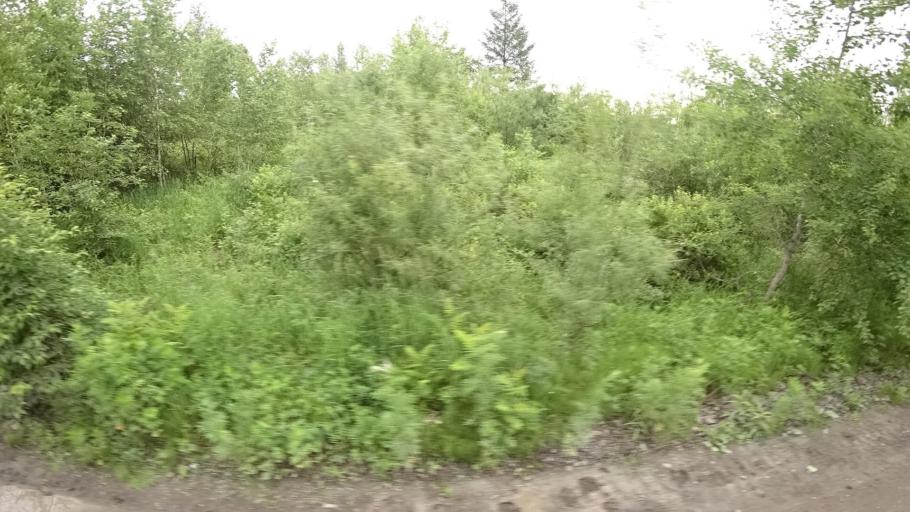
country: RU
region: Khabarovsk Krai
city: Amursk
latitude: 49.9061
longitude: 136.1422
